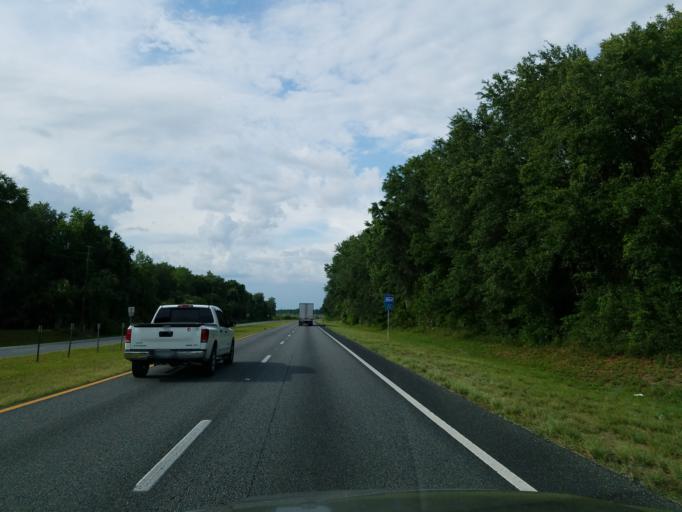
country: US
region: Florida
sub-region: Marion County
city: Citra
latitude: 29.4321
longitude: -82.1099
